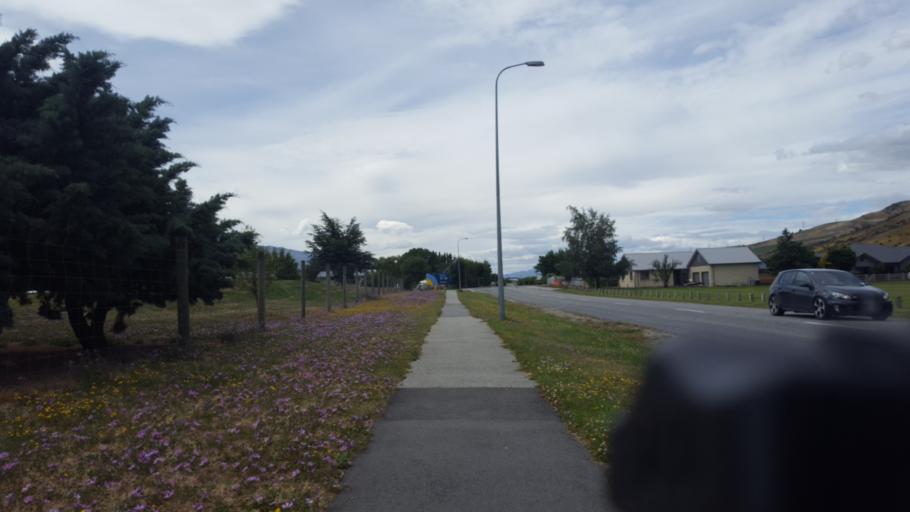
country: NZ
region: Otago
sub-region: Queenstown-Lakes District
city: Wanaka
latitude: -45.0413
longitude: 169.2143
